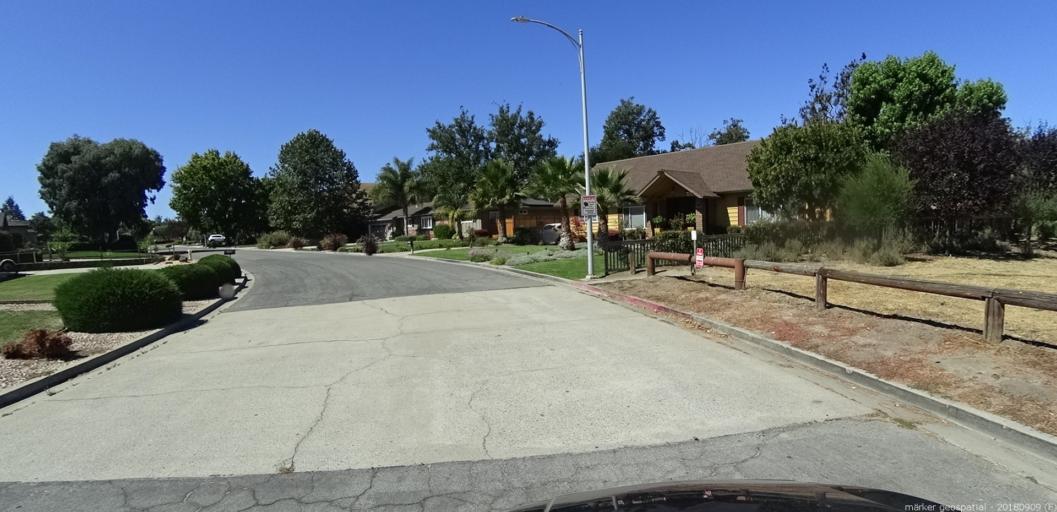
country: US
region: California
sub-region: Monterey County
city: Salinas
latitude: 36.6124
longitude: -121.6928
